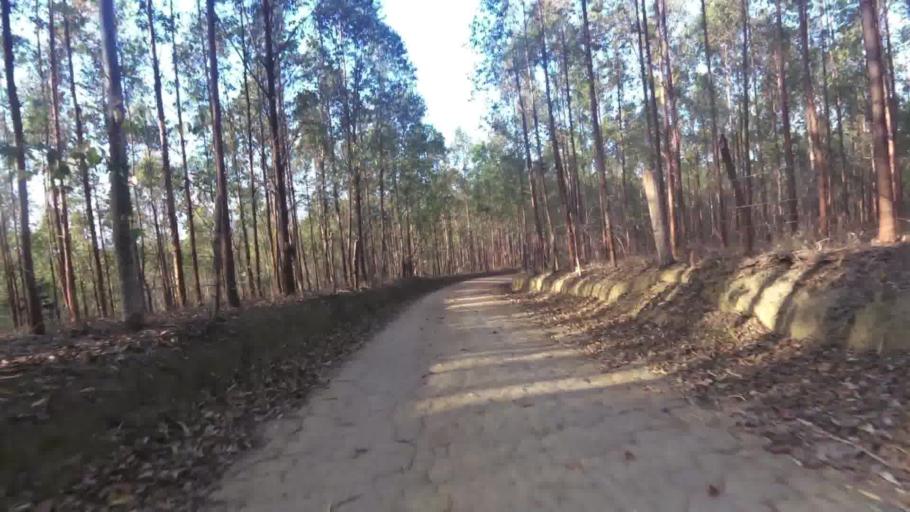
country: BR
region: Espirito Santo
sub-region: Marataizes
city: Marataizes
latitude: -21.1634
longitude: -41.0416
